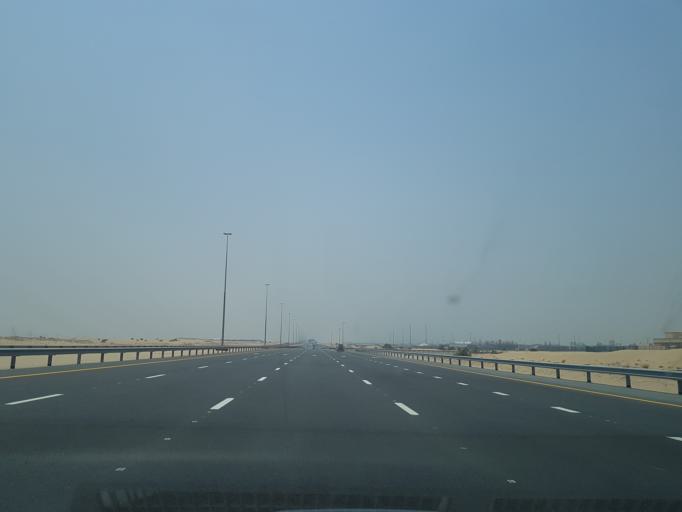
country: AE
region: Dubai
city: Dubai
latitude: 25.0714
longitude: 55.3234
